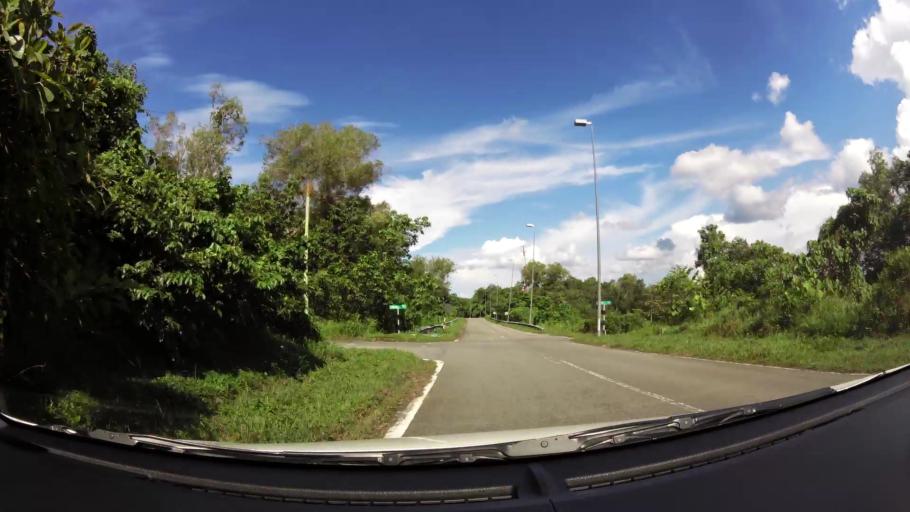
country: BN
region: Brunei and Muara
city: Bandar Seri Begawan
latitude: 4.9511
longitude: 114.9392
